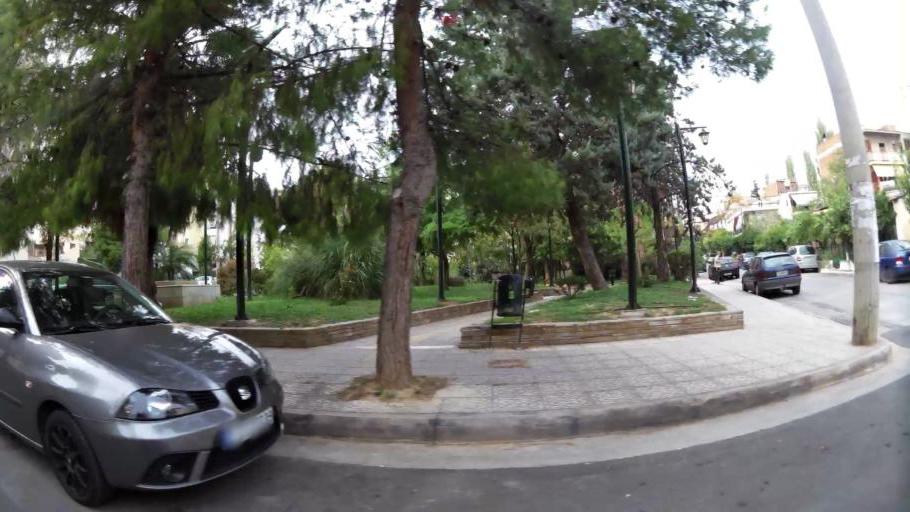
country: GR
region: Attica
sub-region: Nomarchia Athinas
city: Chaidari
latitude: 38.0135
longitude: 23.6643
